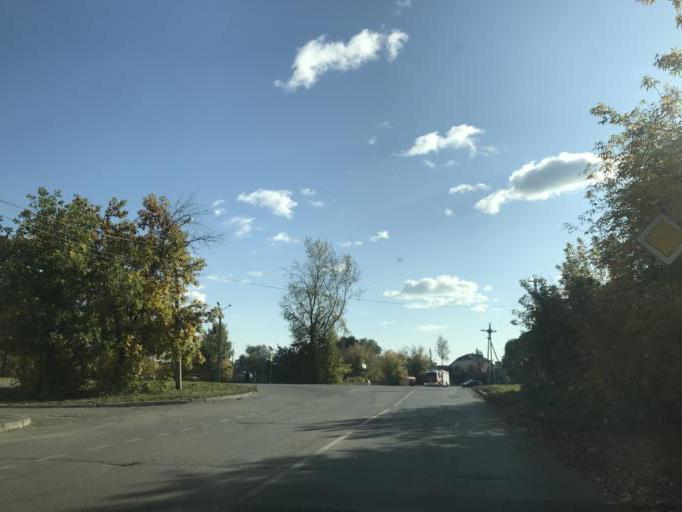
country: RU
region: Chelyabinsk
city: Dolgoderevenskoye
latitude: 55.2587
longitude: 61.3635
